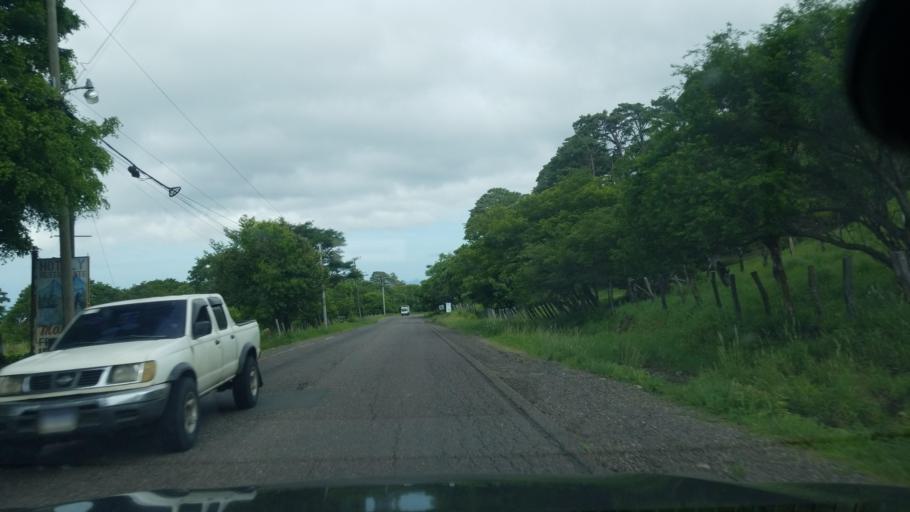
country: HN
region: Choluteca
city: Corpus
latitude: 13.3673
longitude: -86.9540
